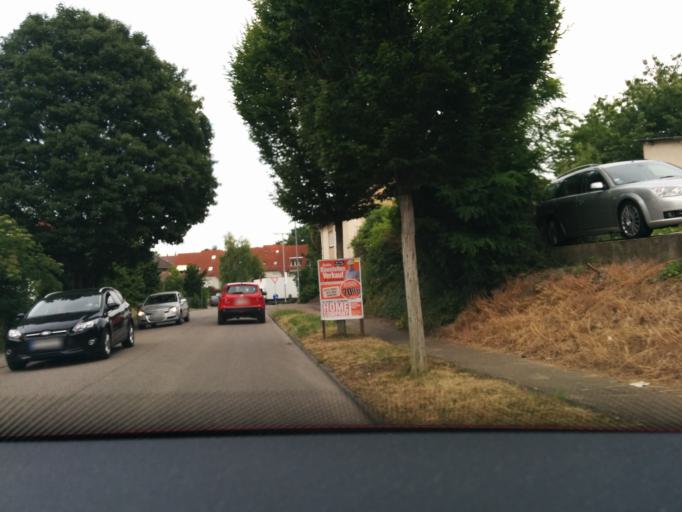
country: DE
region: Baden-Wuerttemberg
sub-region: Regierungsbezirk Stuttgart
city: Ditzingen
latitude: 48.8241
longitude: 9.0691
